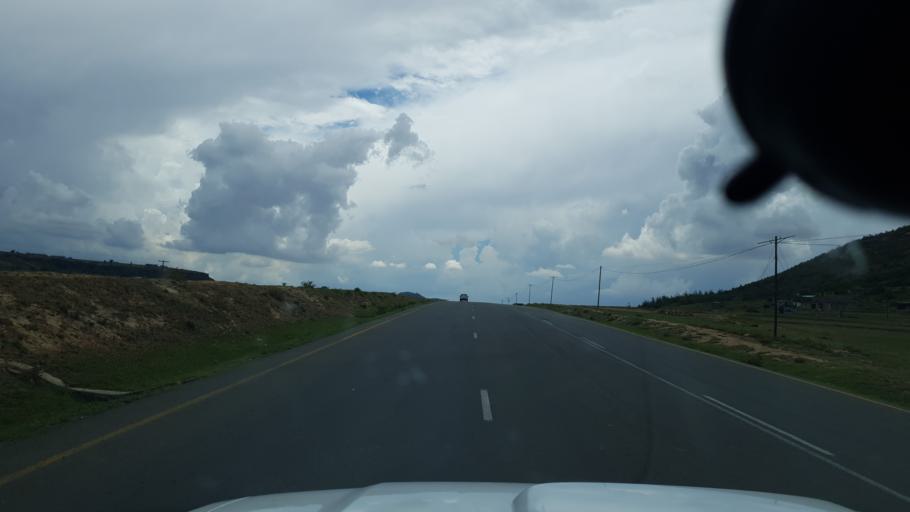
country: LS
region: Maseru
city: Nako
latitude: -29.6037
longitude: 27.4996
